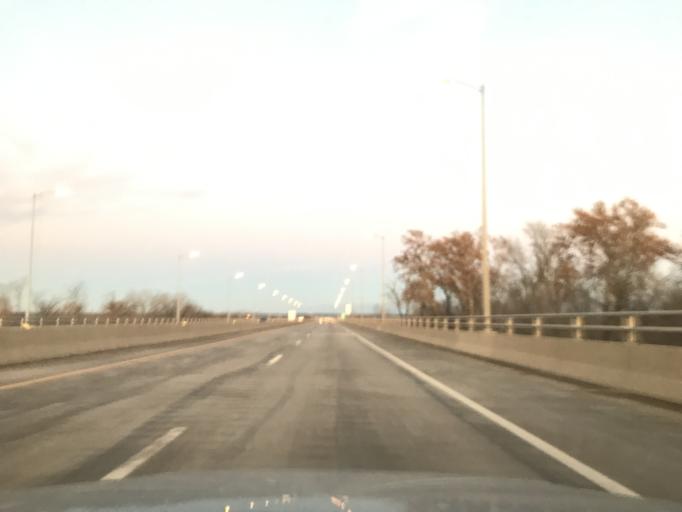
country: US
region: Missouri
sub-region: Marion County
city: Hannibal
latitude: 39.7224
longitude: -91.3516
